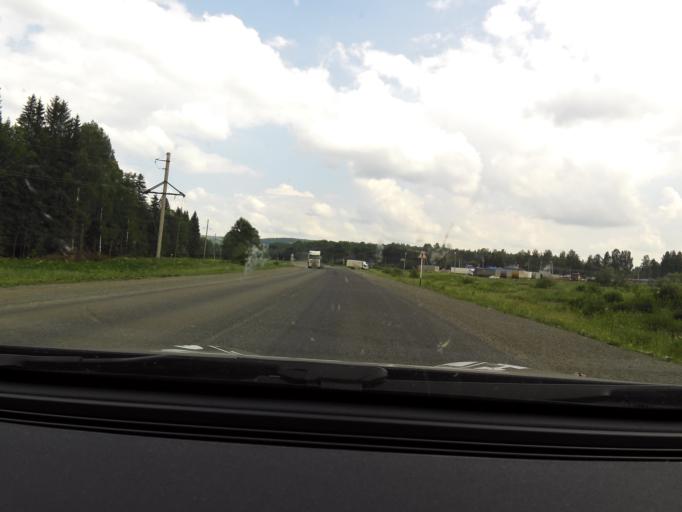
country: RU
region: Sverdlovsk
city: Ufimskiy
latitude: 56.7824
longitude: 58.3989
